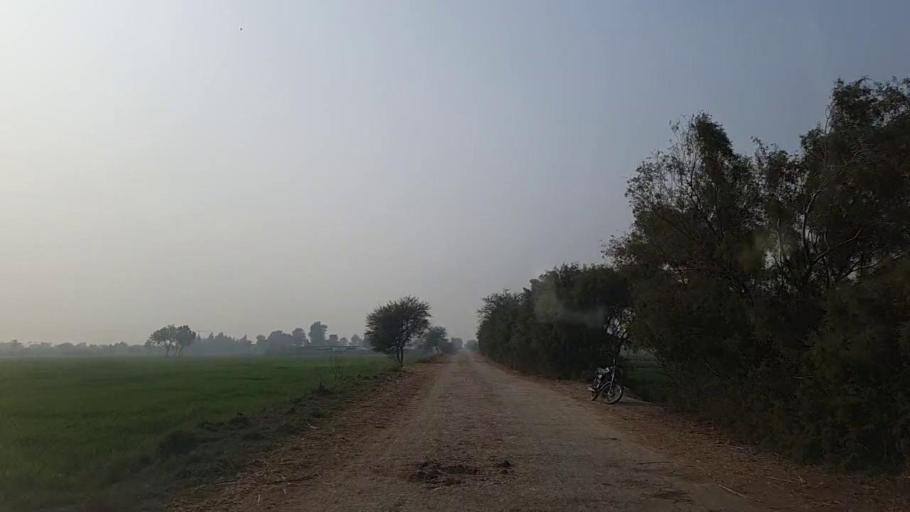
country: PK
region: Sindh
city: Sanghar
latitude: 26.0869
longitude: 68.9239
